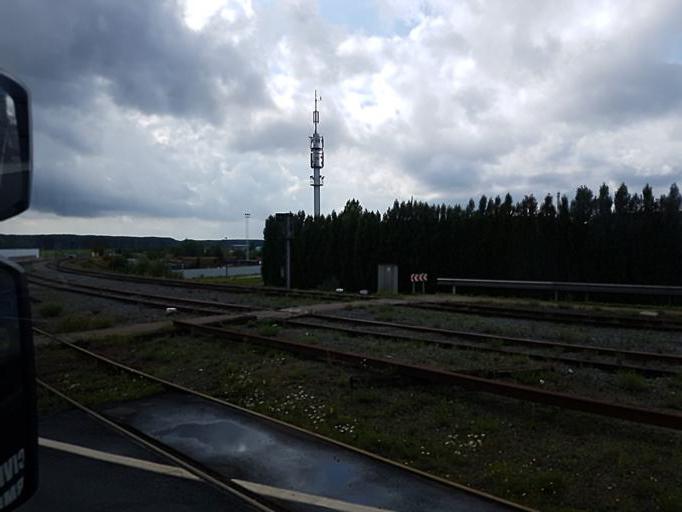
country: BE
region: Flanders
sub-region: Provincie Antwerpen
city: Antwerpen
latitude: 51.2456
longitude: 4.3866
